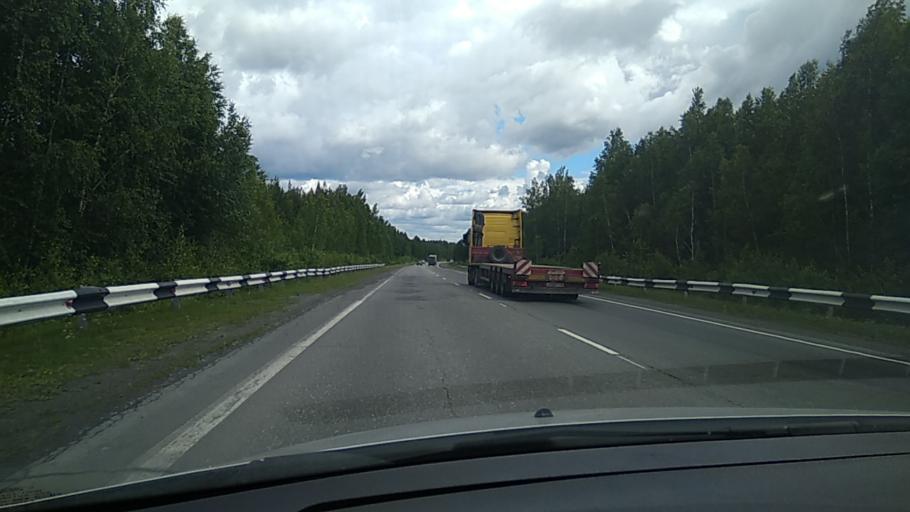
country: RU
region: Sverdlovsk
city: Verkh-Neyvinskiy
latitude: 57.2391
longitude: 60.2695
